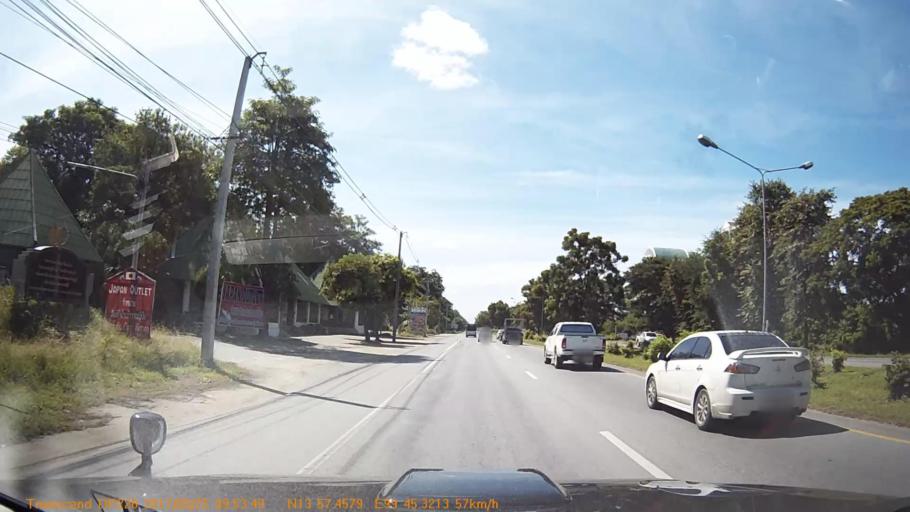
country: TH
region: Kanchanaburi
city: Tha Maka
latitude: 13.9572
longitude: 99.7555
